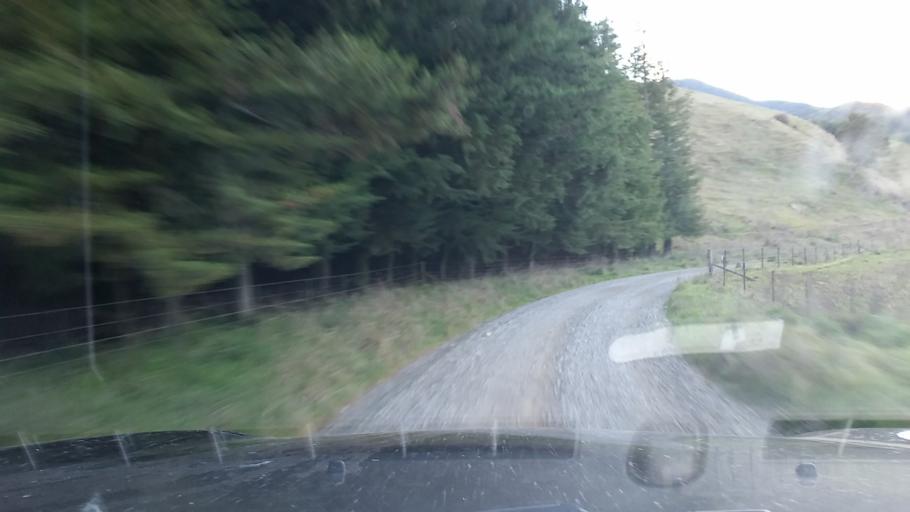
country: NZ
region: Marlborough
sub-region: Marlborough District
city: Blenheim
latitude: -41.5054
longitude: 173.5906
